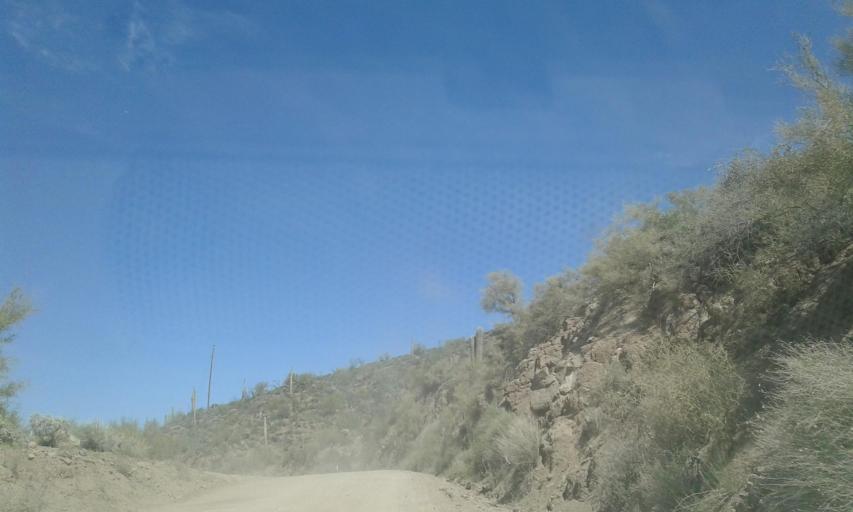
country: US
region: Arizona
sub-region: Gila County
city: Tonto Basin
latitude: 33.6071
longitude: -111.1977
